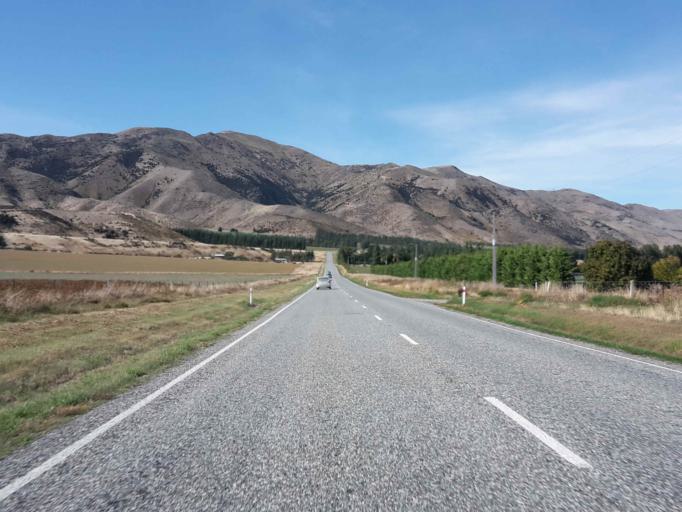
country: NZ
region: Otago
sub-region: Queenstown-Lakes District
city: Wanaka
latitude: -44.7380
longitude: 169.3249
